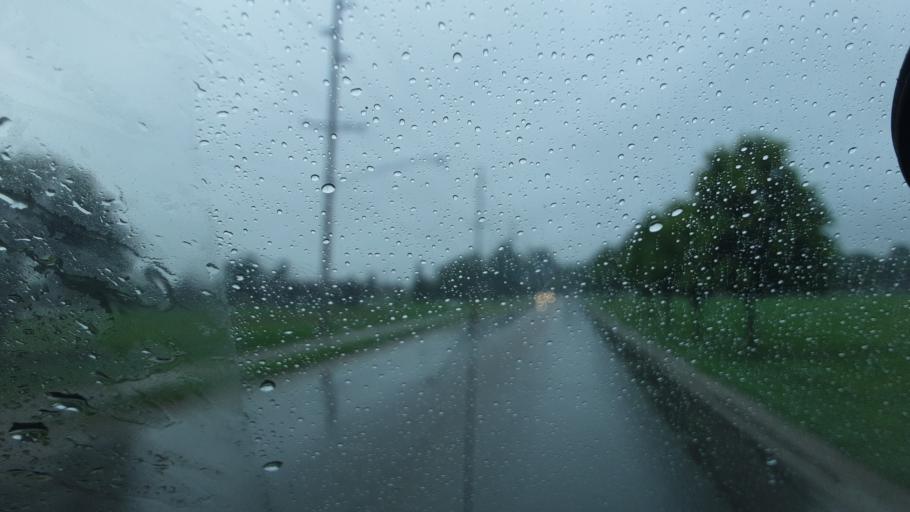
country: US
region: Indiana
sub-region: Adams County
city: Berne
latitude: 40.6544
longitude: -84.9644
